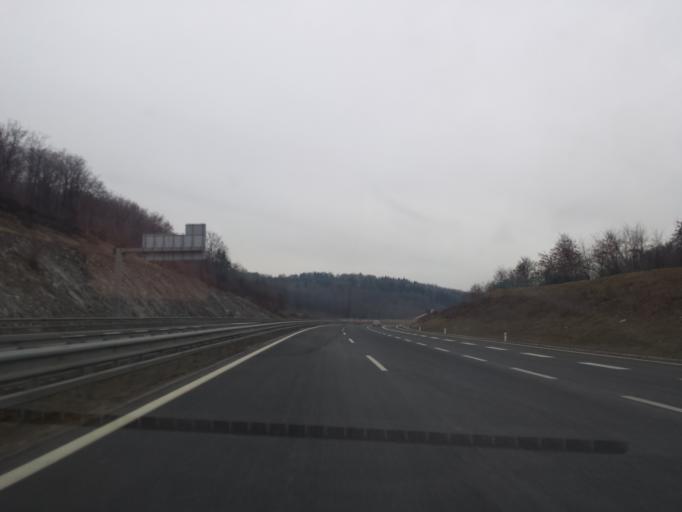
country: SI
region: Novo Mesto
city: Novo Mesto
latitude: 45.8444
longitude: 15.1523
